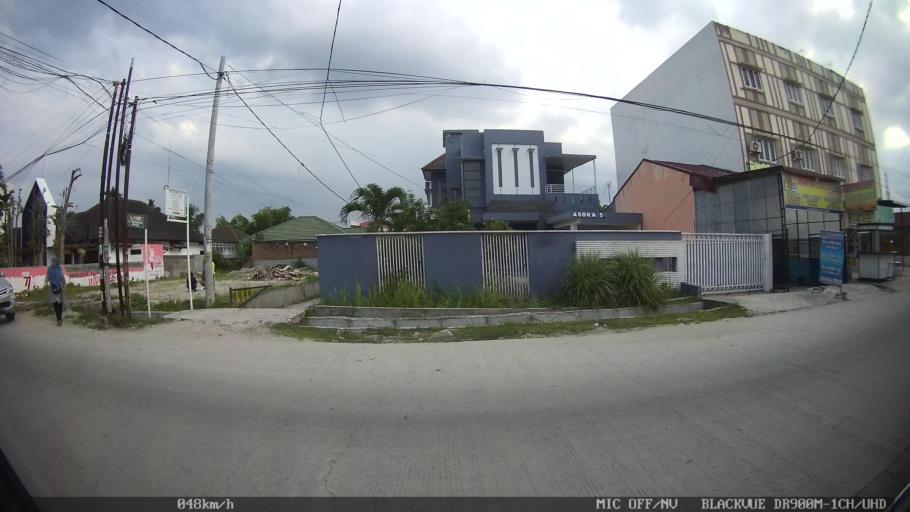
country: ID
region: North Sumatra
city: Sunggal
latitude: 3.5628
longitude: 98.6202
